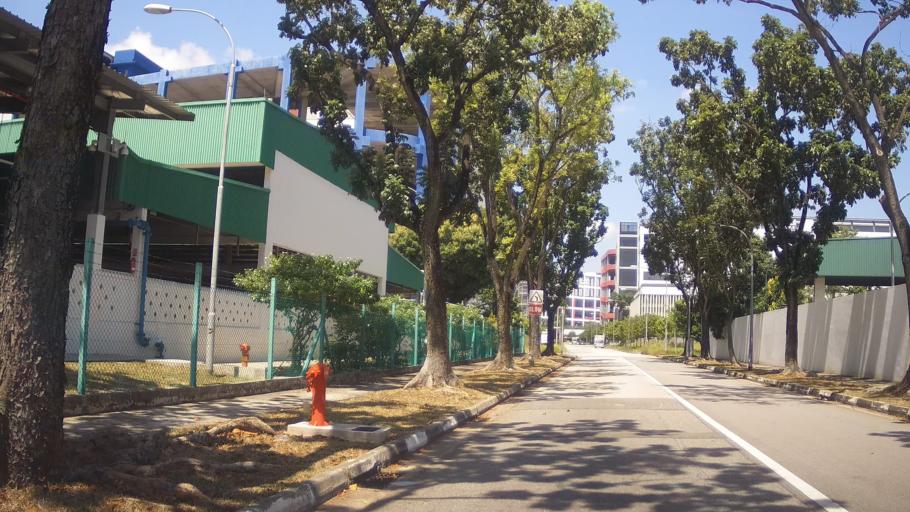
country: SG
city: Singapore
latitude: 1.3145
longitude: 103.7258
